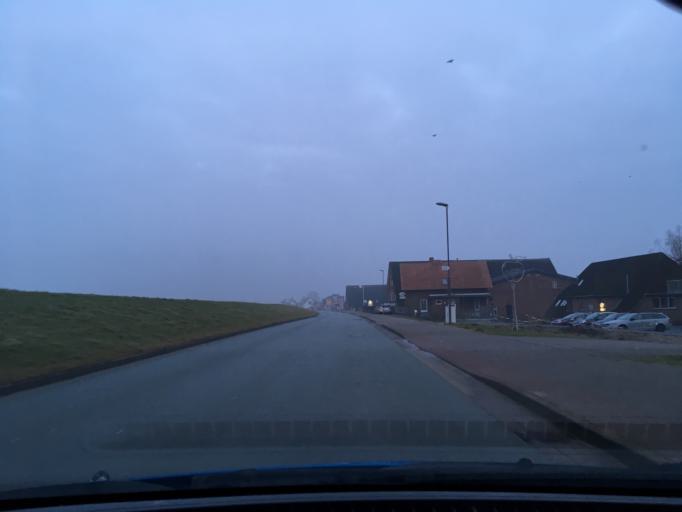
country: DE
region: Lower Saxony
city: Stelle
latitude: 53.3962
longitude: 10.1683
